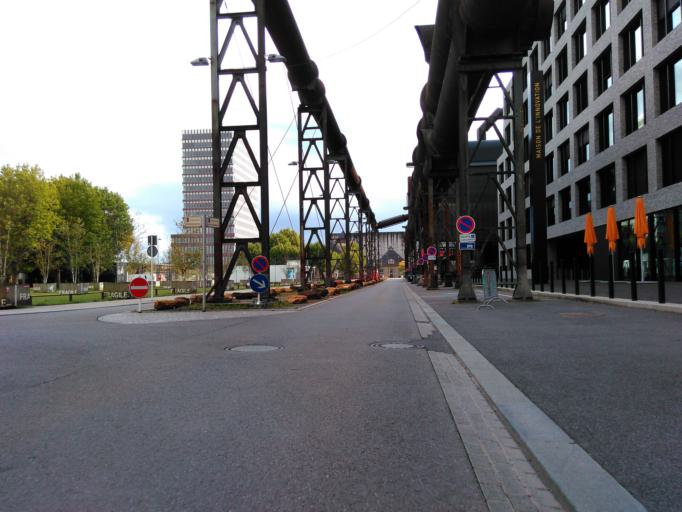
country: FR
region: Lorraine
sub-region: Departement de la Moselle
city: Russange
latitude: 49.5021
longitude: 5.9494
